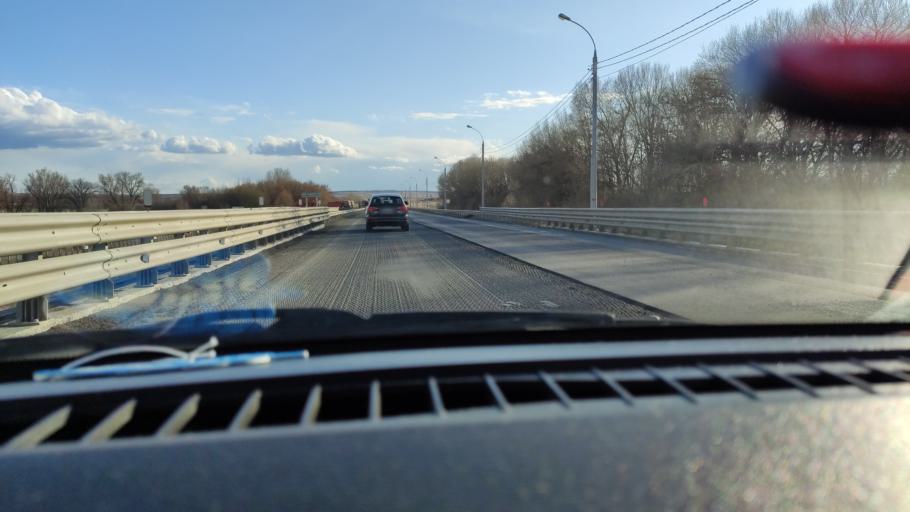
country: RU
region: Saratov
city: Yelshanka
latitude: 51.8222
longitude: 46.2175
